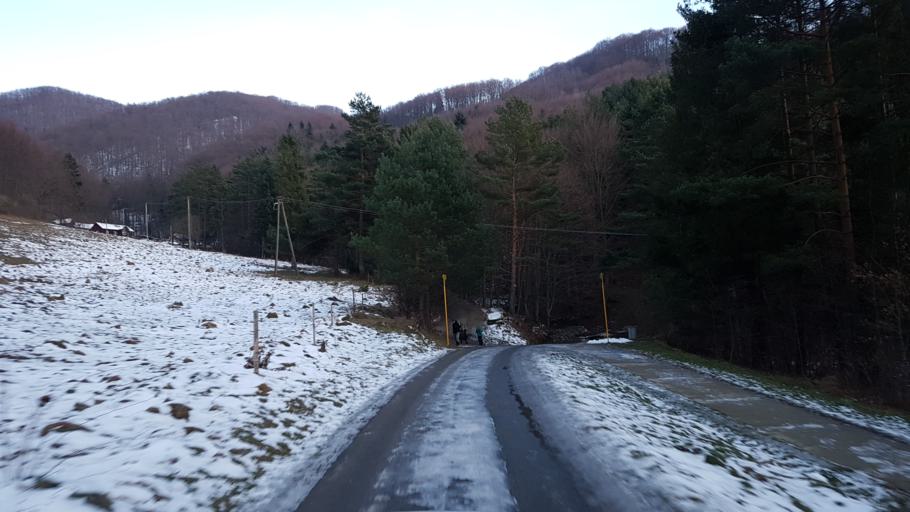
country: PL
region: Lesser Poland Voivodeship
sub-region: Powiat nowosadecki
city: Rytro
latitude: 49.4890
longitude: 20.6903
